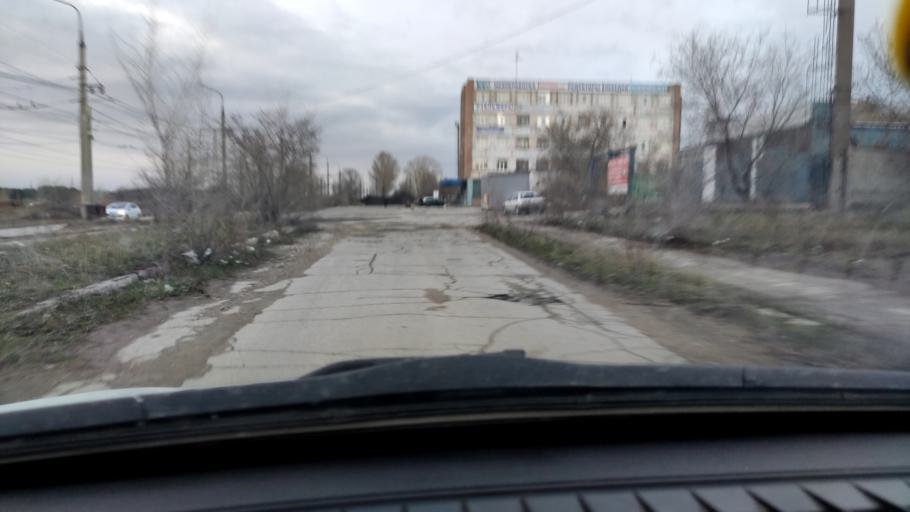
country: RU
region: Samara
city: Zhigulevsk
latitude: 53.4870
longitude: 49.5093
